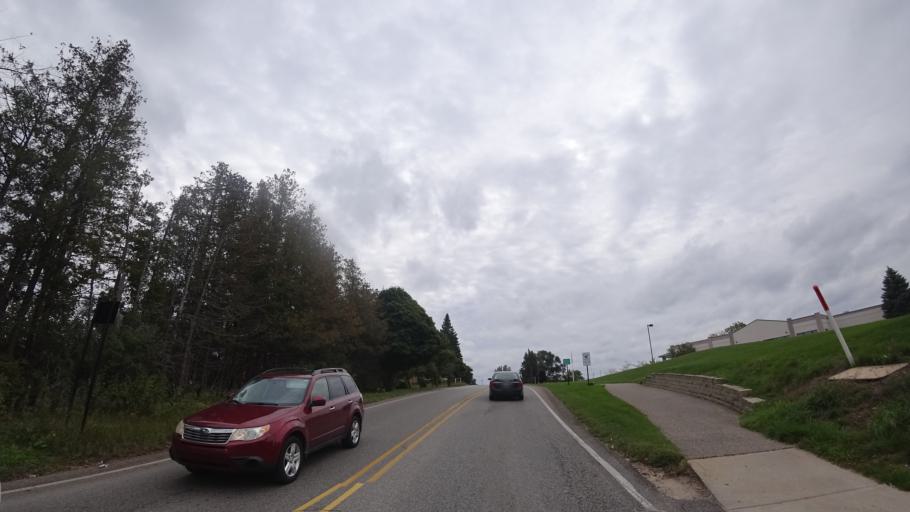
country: US
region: Michigan
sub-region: Emmet County
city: Petoskey
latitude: 45.3595
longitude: -84.9709
